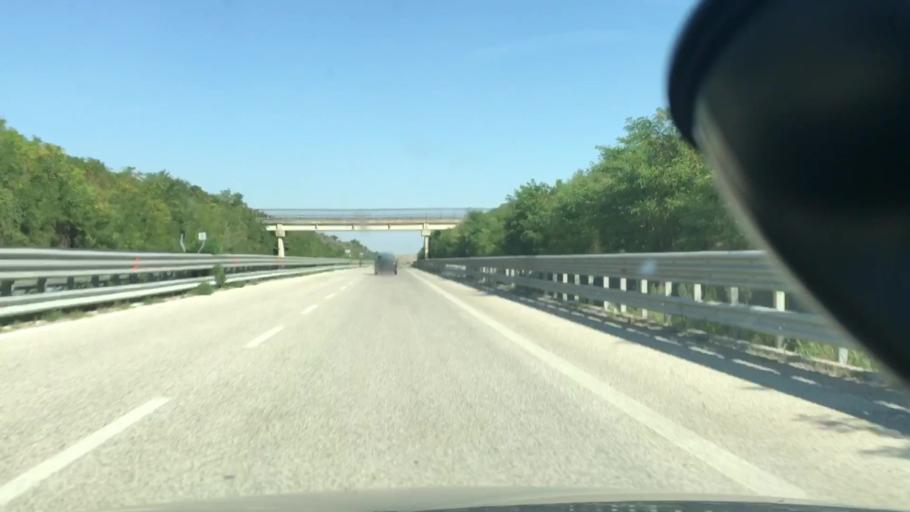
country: IT
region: Apulia
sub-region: Provincia di Foggia
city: Ordona
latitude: 41.2908
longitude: 15.5540
